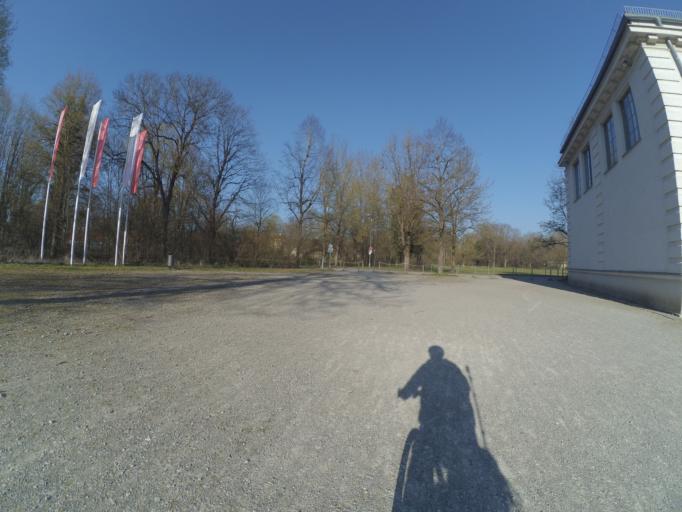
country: DE
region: Bavaria
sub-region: Upper Bavaria
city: Oberschleissheim
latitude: 48.2463
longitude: 11.5573
